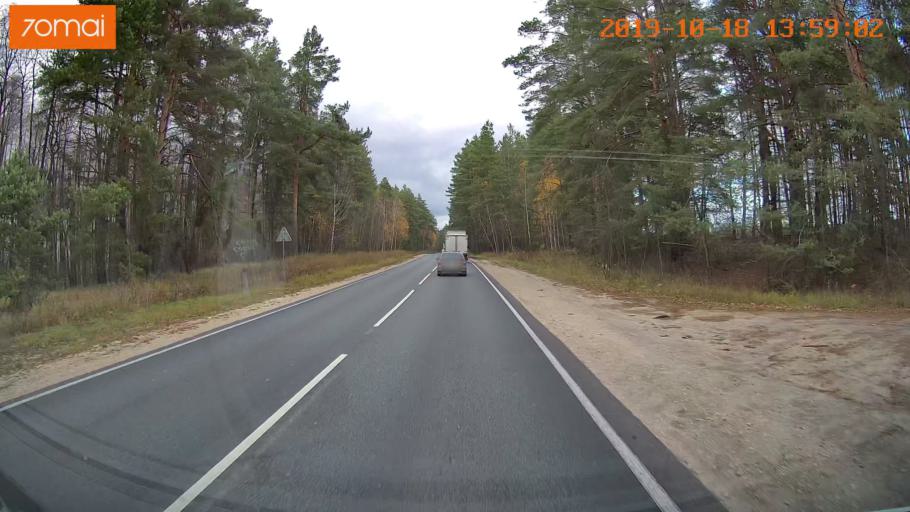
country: RU
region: Rjazan
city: Spas-Klepiki
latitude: 55.0905
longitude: 40.0594
